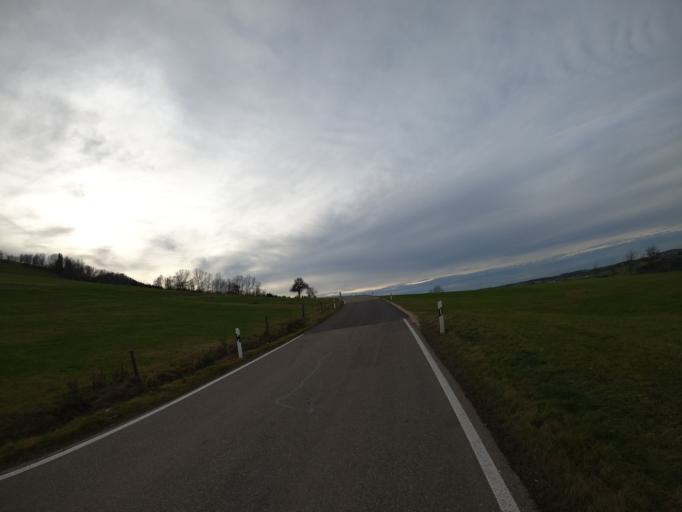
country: DE
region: Baden-Wuerttemberg
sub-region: Regierungsbezirk Stuttgart
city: Ottenbach
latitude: 48.7541
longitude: 9.7256
